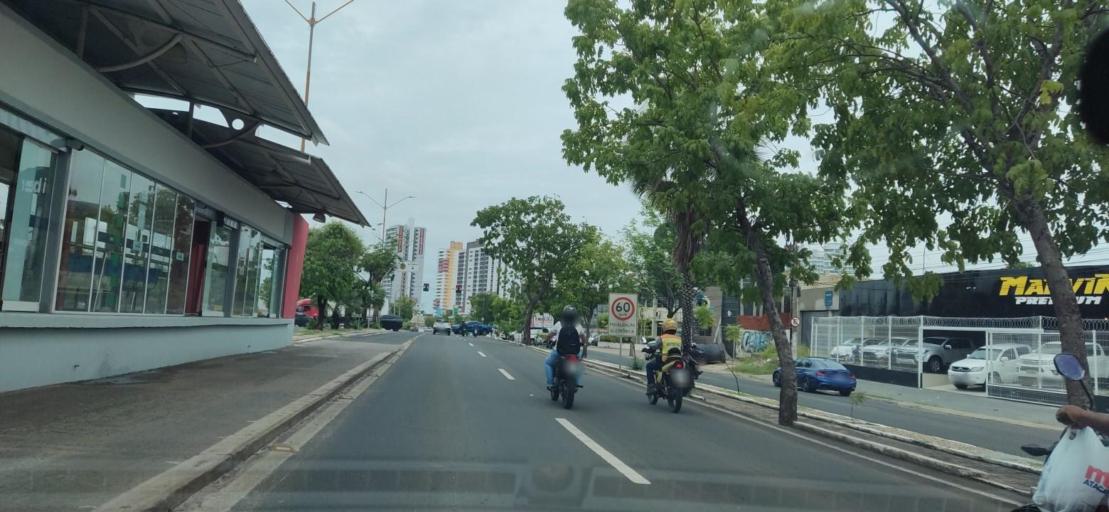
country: BR
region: Piaui
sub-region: Teresina
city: Teresina
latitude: -5.0803
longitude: -42.7861
